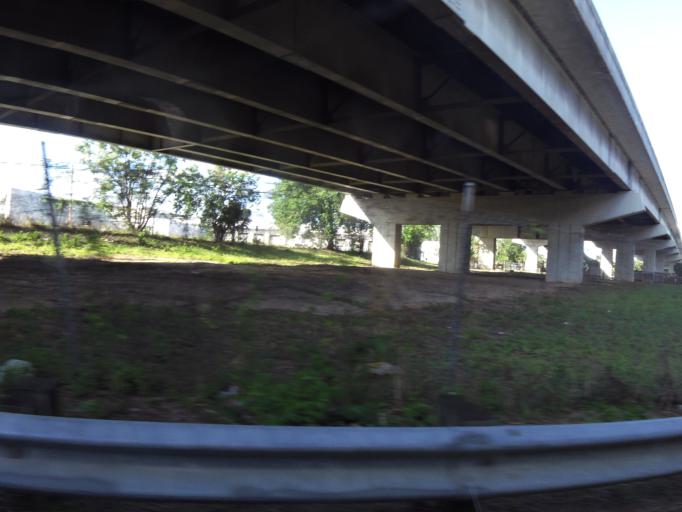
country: US
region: Florida
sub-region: Duval County
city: Jacksonville
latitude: 30.3279
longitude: -81.6782
